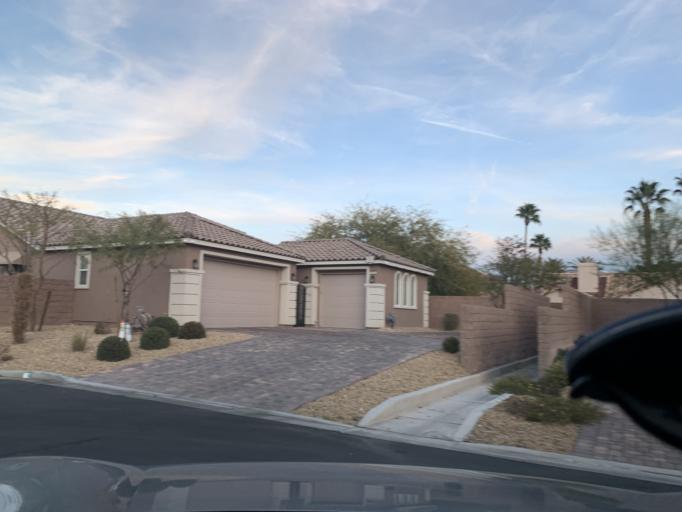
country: US
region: Nevada
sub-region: Clark County
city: Spring Valley
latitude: 36.0903
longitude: -115.2331
